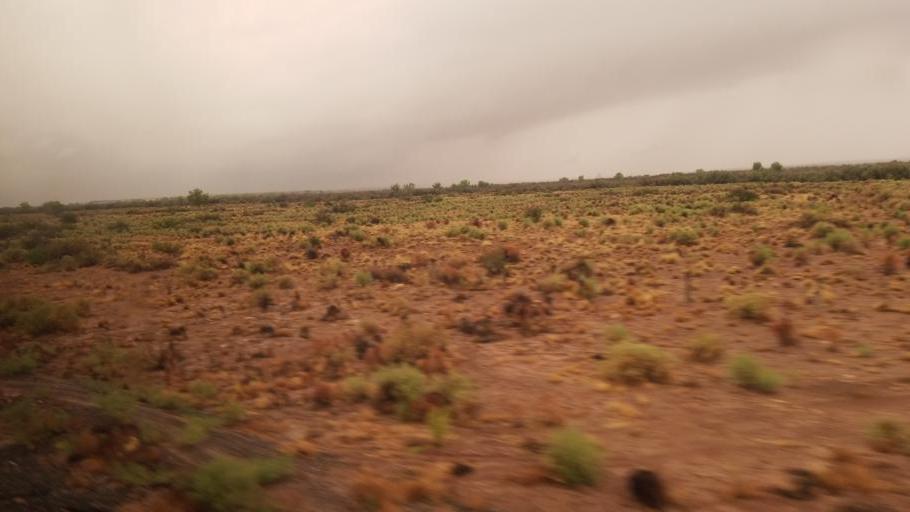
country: US
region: Arizona
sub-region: Navajo County
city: Joseph City
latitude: 34.9673
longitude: -110.4384
